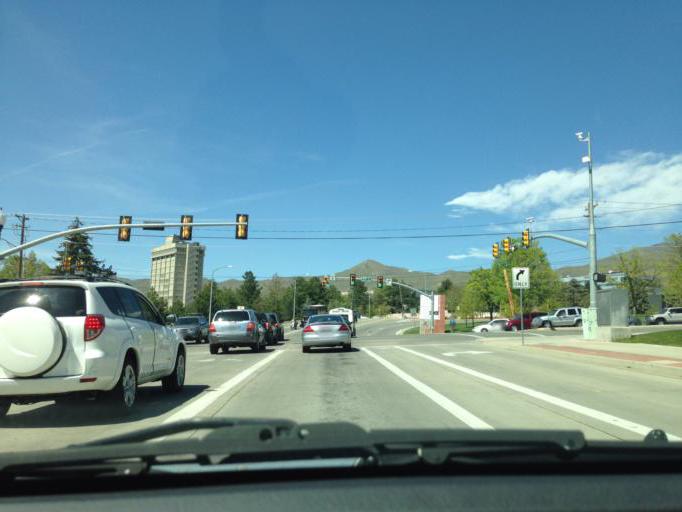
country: US
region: Utah
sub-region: Salt Lake County
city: Salt Lake City
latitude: 40.7580
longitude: -111.8453
